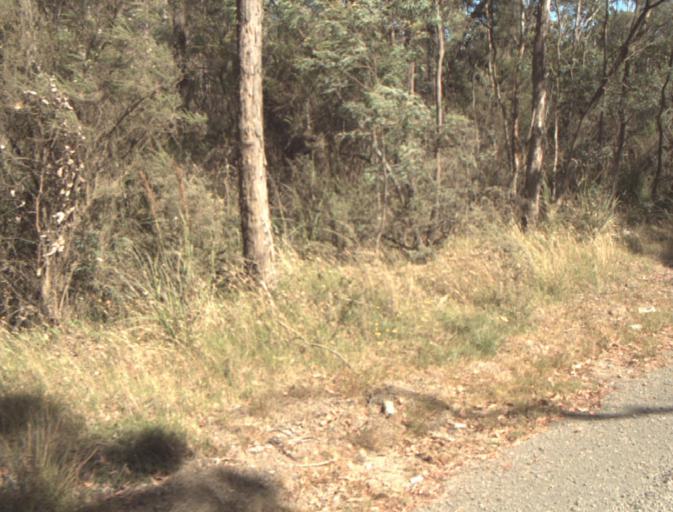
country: AU
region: Tasmania
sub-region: Launceston
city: Mayfield
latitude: -41.3461
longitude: 147.2152
